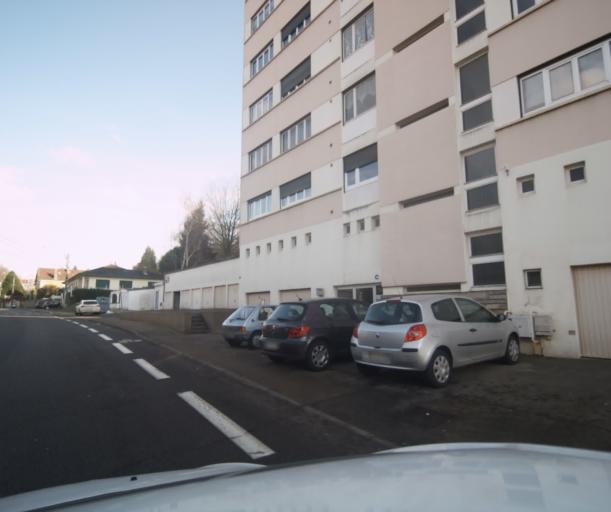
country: FR
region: Franche-Comte
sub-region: Departement du Doubs
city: Besancon
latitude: 47.2489
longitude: 6.0475
